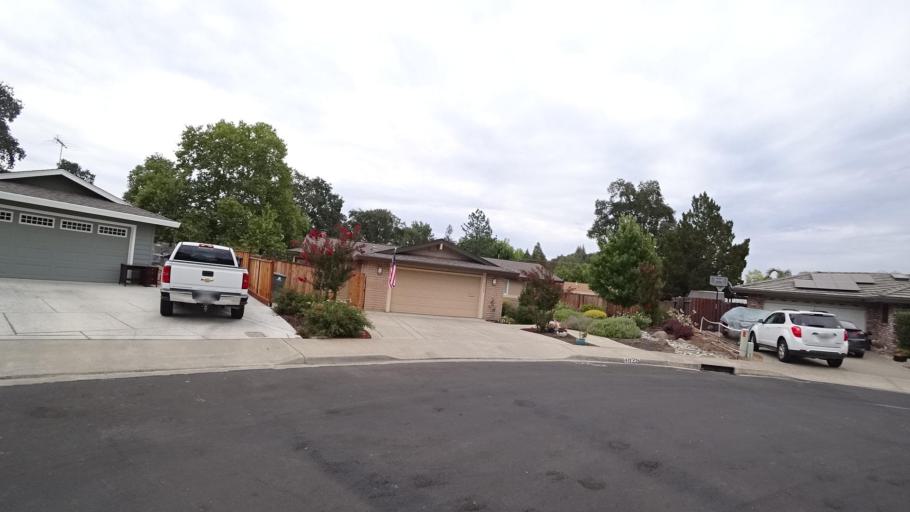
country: US
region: California
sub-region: Placer County
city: Rocklin
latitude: 38.7979
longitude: -121.2523
